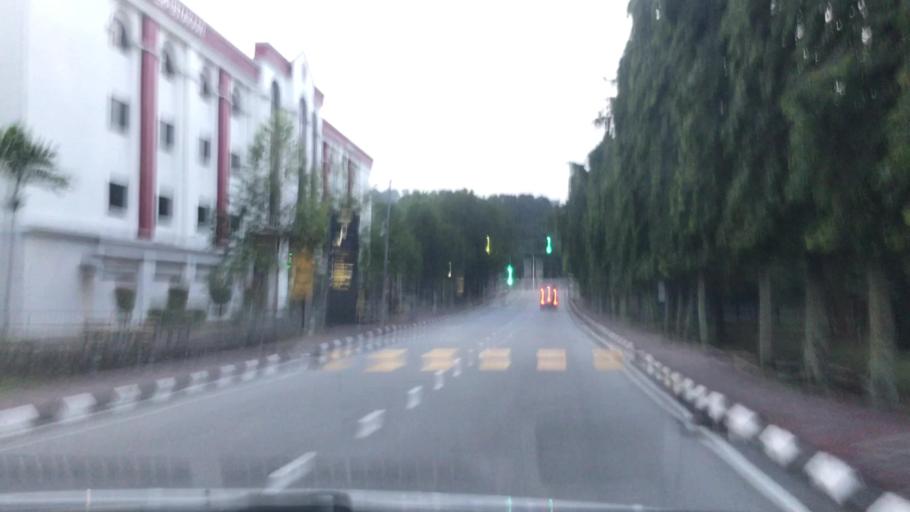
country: MY
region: Kuala Lumpur
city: Kuala Lumpur
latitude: 3.1197
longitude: 101.6546
